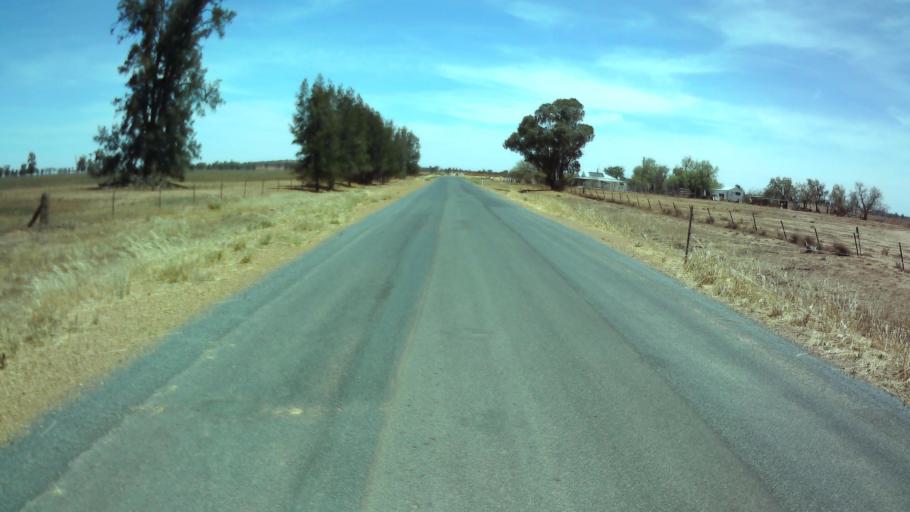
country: AU
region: New South Wales
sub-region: Weddin
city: Grenfell
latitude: -33.7485
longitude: 147.7676
